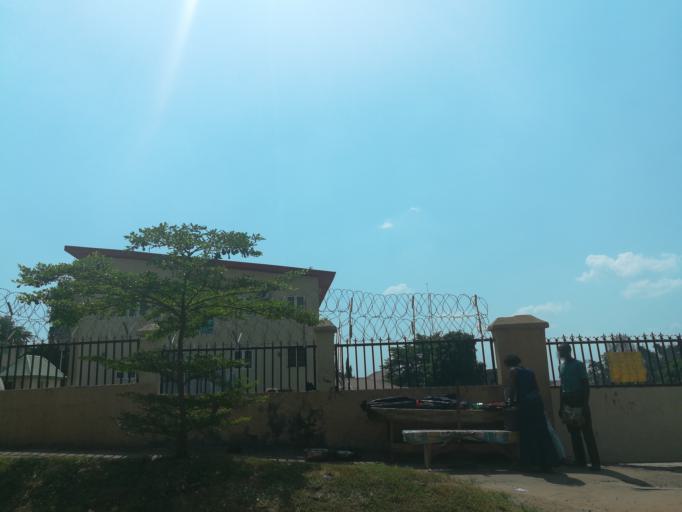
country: NG
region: Abuja Federal Capital Territory
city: Abuja
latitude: 9.0657
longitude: 7.4368
